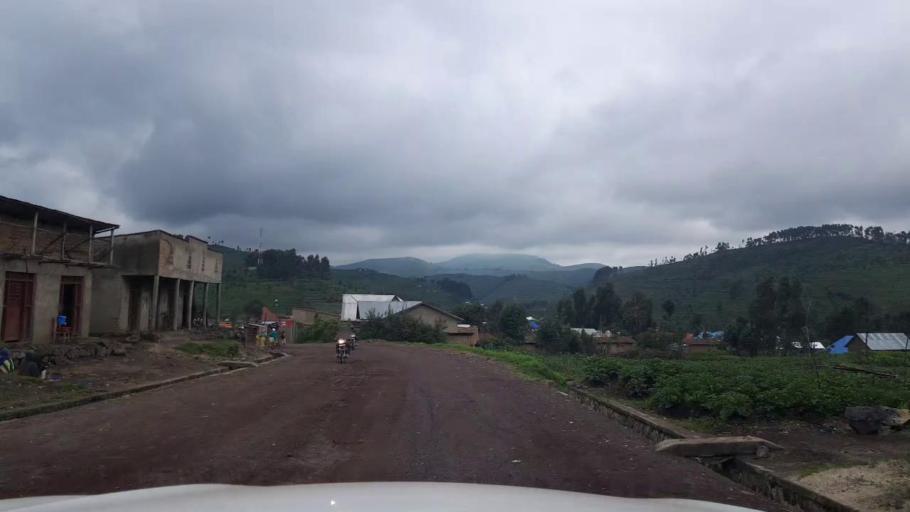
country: RW
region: Northern Province
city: Musanze
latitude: -1.6084
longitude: 29.4519
